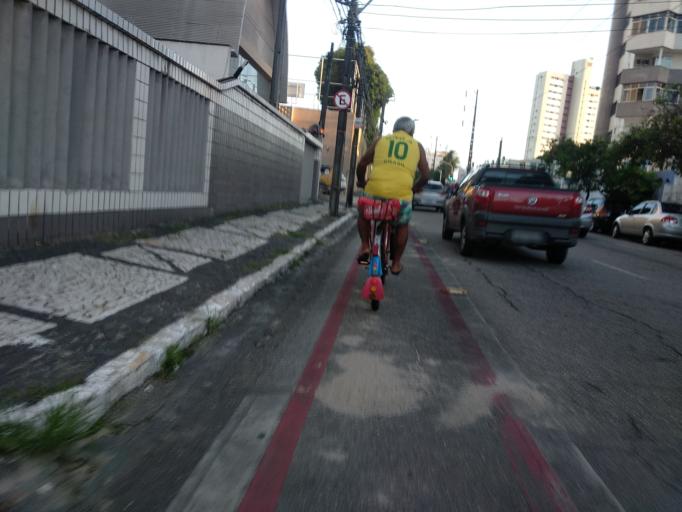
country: BR
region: Ceara
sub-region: Fortaleza
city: Fortaleza
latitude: -3.7411
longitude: -38.5110
